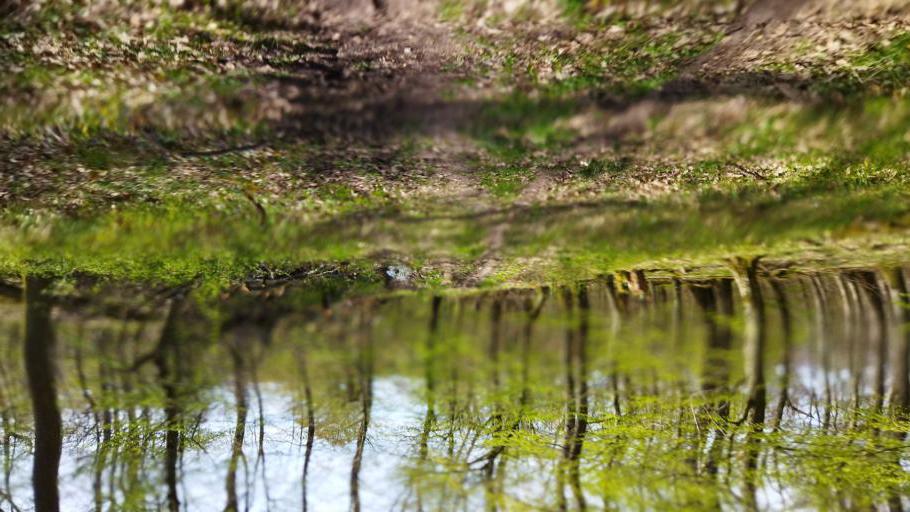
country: DE
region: Baden-Wuerttemberg
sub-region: Regierungsbezirk Stuttgart
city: Zaberfeld
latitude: 49.0206
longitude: 8.9372
